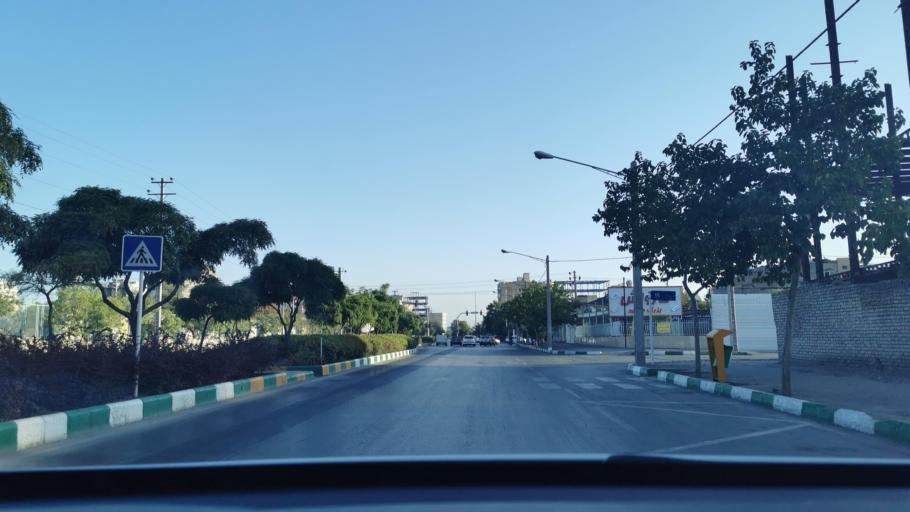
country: IR
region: Razavi Khorasan
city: Mashhad
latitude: 36.3507
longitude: 59.5138
